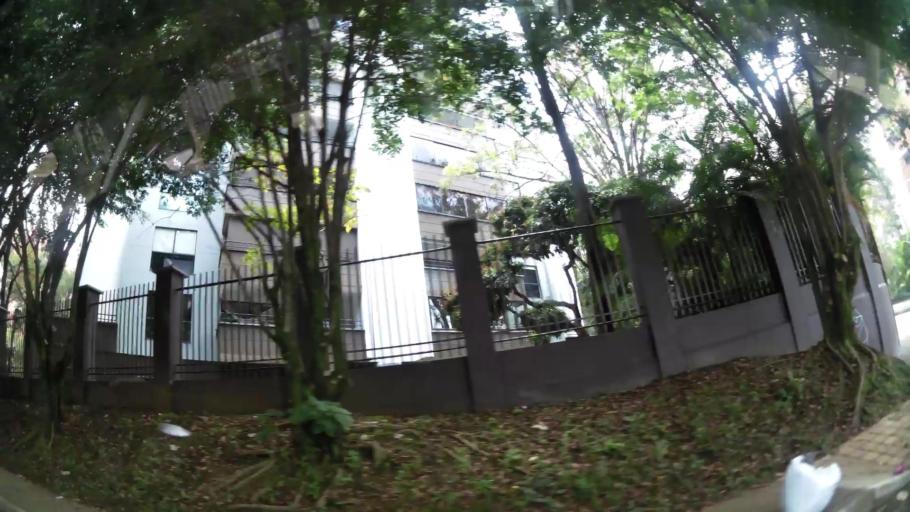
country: CO
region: Antioquia
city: Envigado
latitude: 6.1938
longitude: -75.5699
